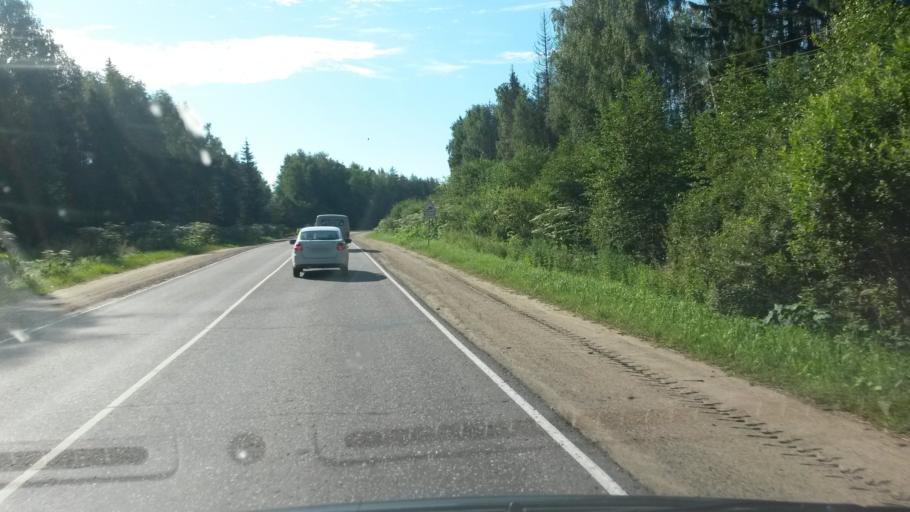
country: RU
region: Ivanovo
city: Novo-Talitsy
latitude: 57.0545
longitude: 40.7316
